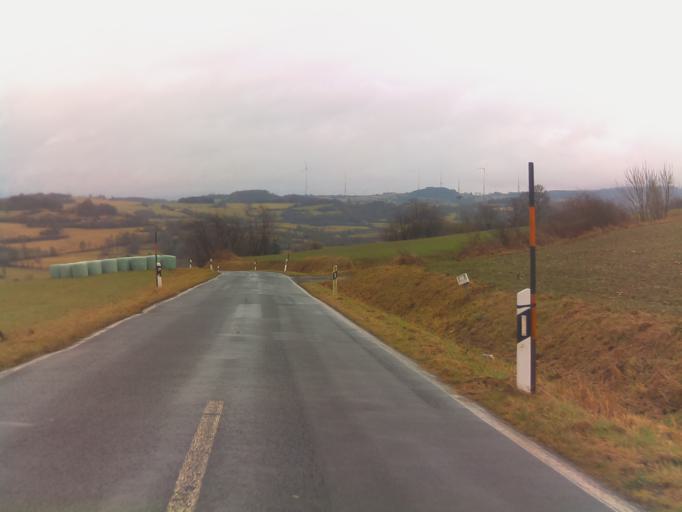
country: DE
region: Hesse
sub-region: Regierungsbezirk Giessen
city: Schotten
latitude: 50.5677
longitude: 9.1072
